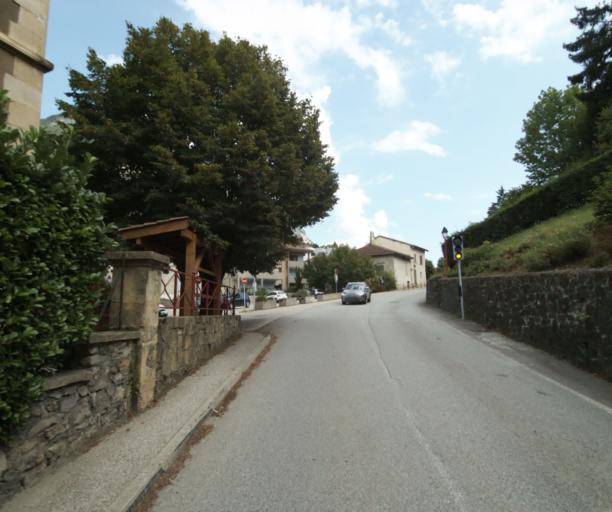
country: FR
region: Rhone-Alpes
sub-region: Departement de l'Isere
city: Corenc
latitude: 45.2196
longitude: 5.7621
